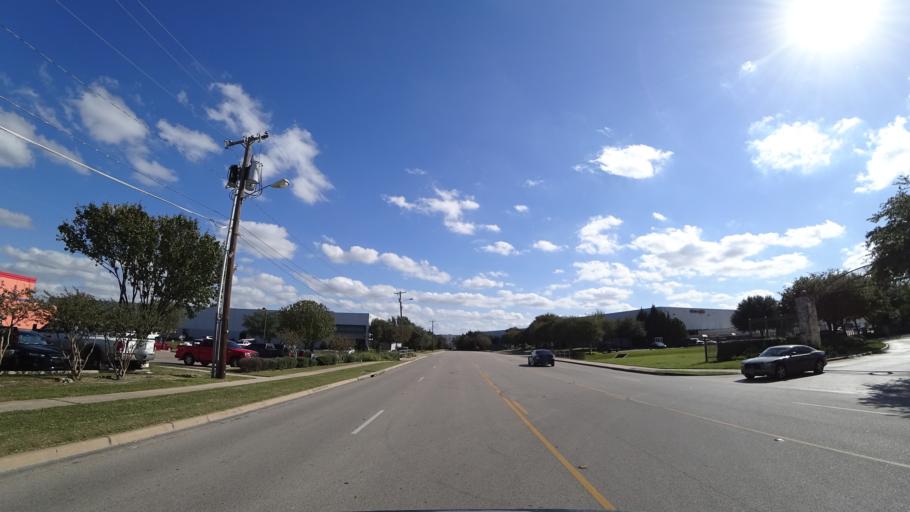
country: US
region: Texas
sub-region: Williamson County
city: Round Rock
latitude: 30.4779
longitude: -97.6798
